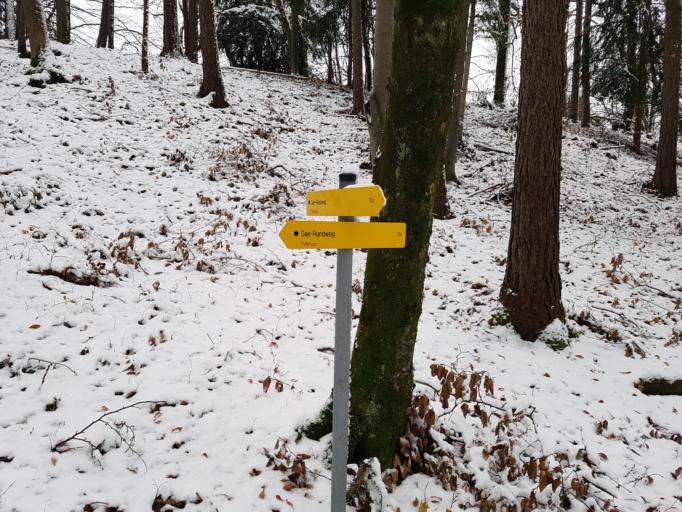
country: AT
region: Salzburg
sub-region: Politischer Bezirk Salzburg-Umgebung
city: Elsbethen
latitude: 47.7410
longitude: 13.0914
